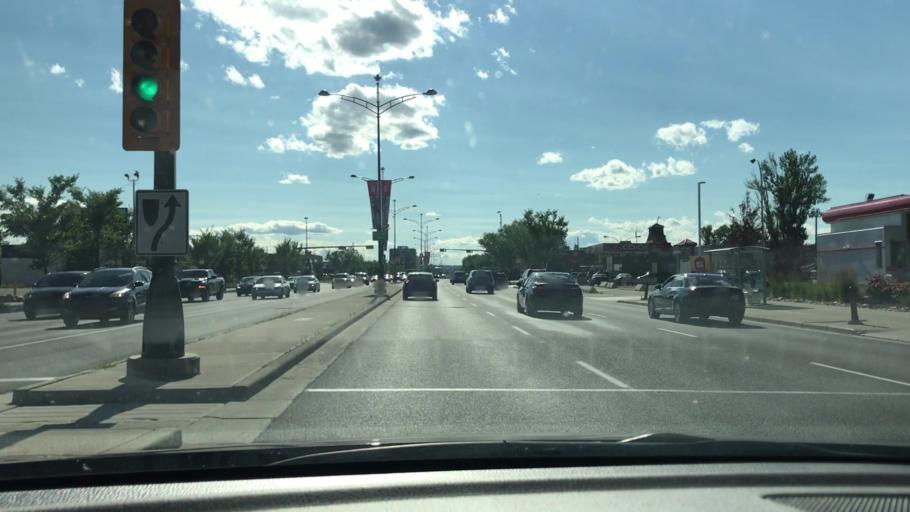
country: CA
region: Alberta
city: Calgary
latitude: 51.0670
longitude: -114.0485
